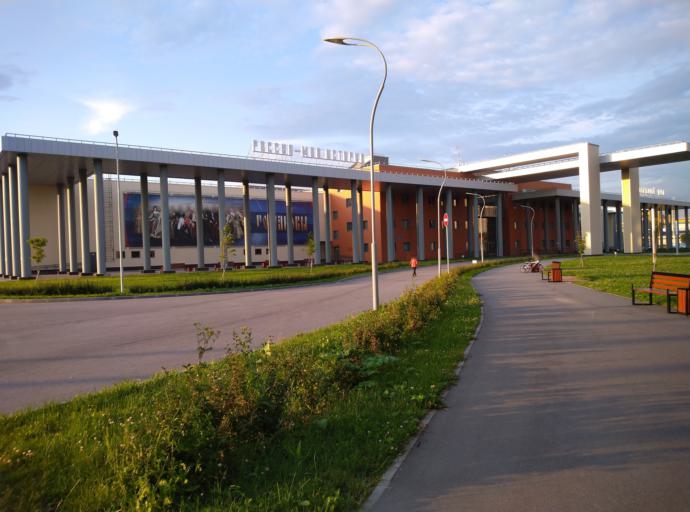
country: RU
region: St.-Petersburg
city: Kupchino
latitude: 59.8647
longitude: 30.3388
